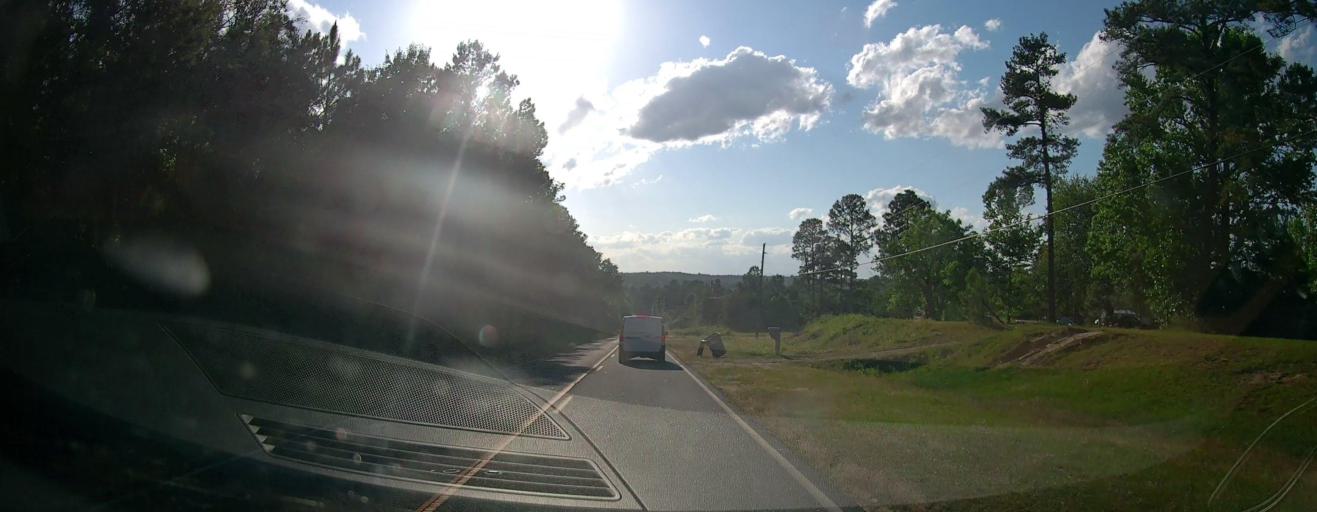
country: US
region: Georgia
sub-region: Peach County
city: Byron
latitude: 32.6765
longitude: -83.7692
